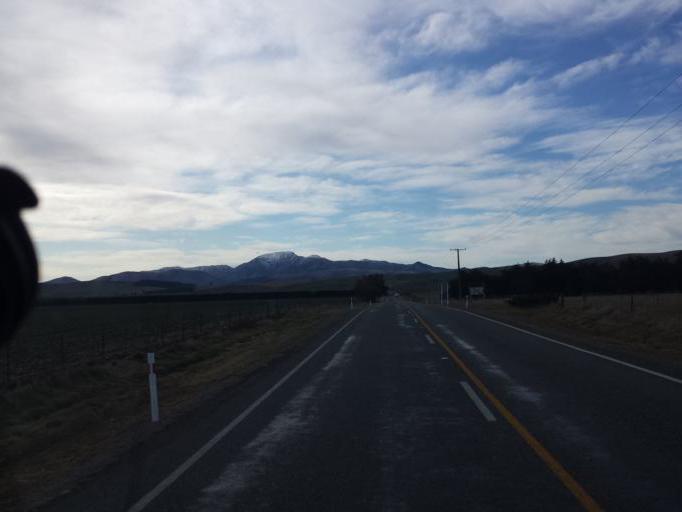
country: NZ
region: Canterbury
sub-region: Timaru District
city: Pleasant Point
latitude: -44.0930
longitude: 170.8525
